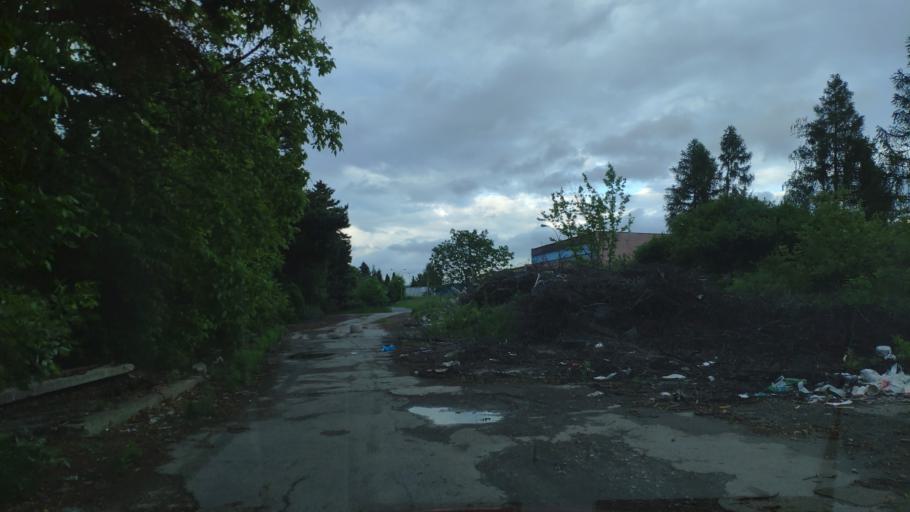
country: SK
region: Kosicky
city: Kosice
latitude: 48.6993
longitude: 21.2439
